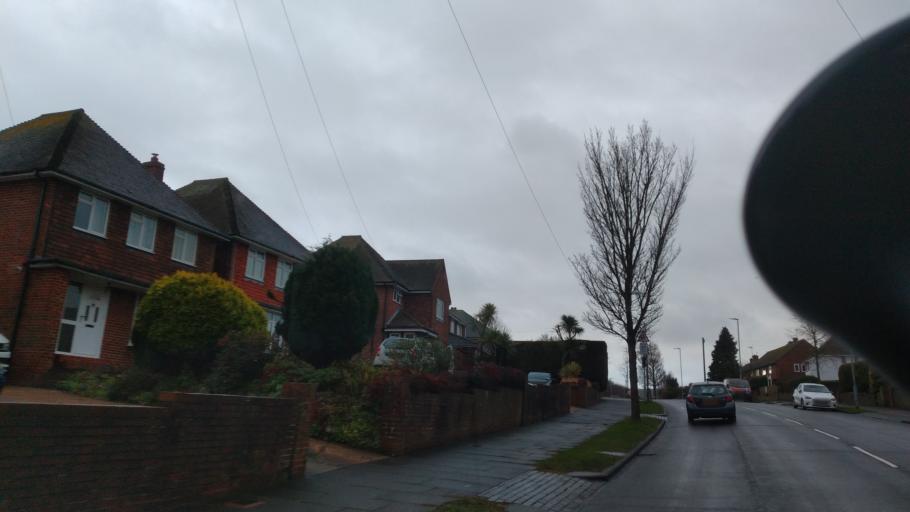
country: GB
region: England
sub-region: East Sussex
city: Eastbourne
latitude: 50.7875
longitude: 0.2557
